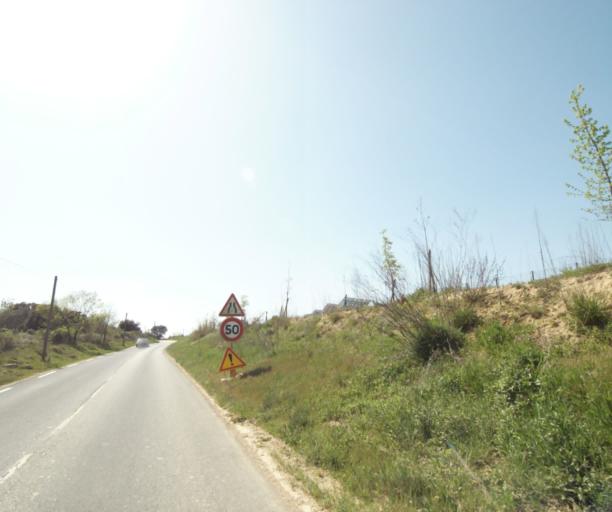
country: FR
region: Languedoc-Roussillon
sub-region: Departement de l'Herault
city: Combaillaux
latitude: 43.6446
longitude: 3.7635
